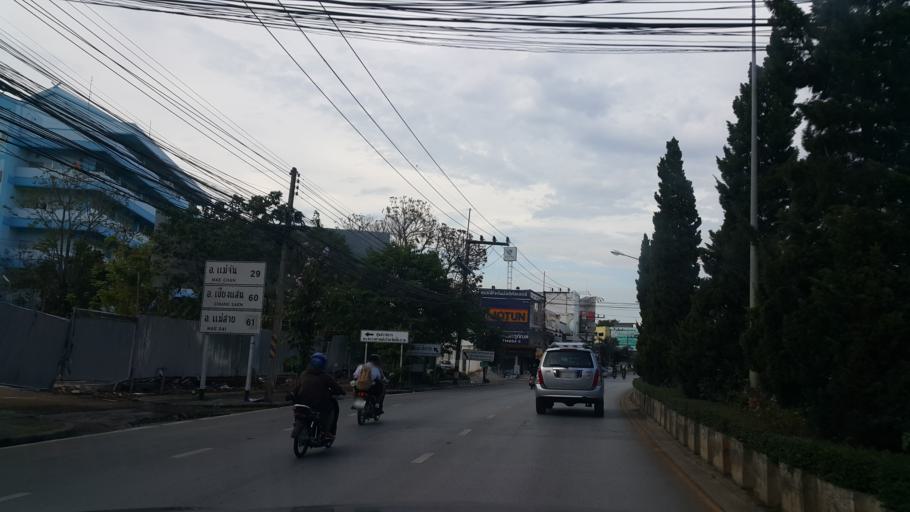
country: TH
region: Chiang Rai
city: Chiang Rai
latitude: 19.9121
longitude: 99.8411
